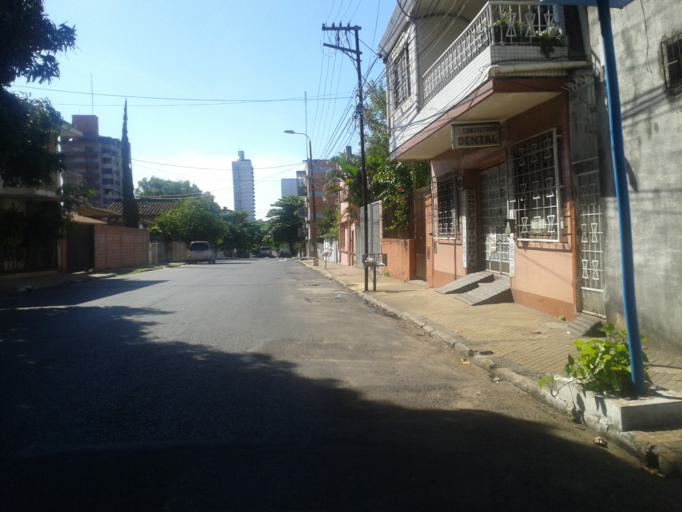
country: PY
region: Asuncion
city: Asuncion
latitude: -25.2923
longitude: -57.6423
